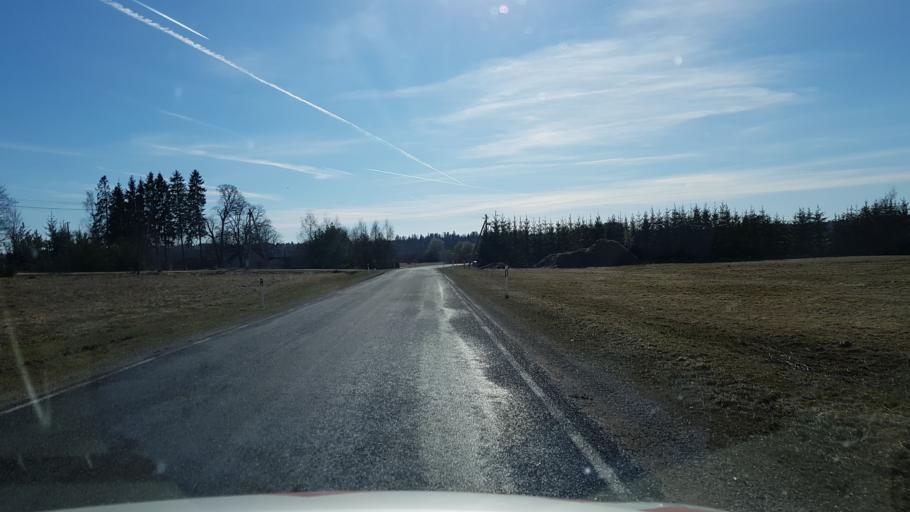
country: EE
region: Laeaene-Virumaa
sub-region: Vinni vald
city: Vinni
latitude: 59.3020
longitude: 26.5458
